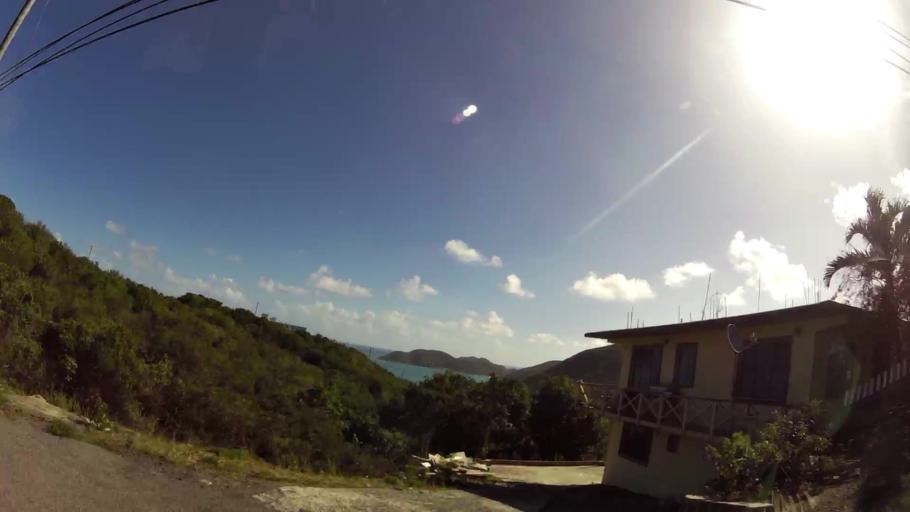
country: VG
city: Tortola
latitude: 18.4889
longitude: -64.3878
